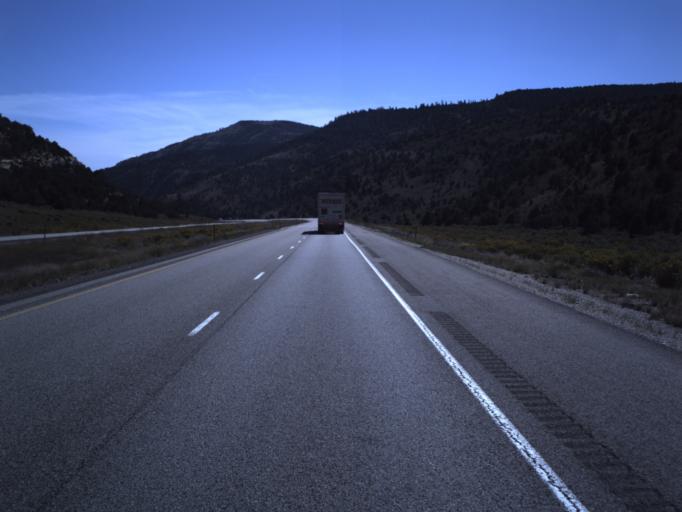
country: US
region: Utah
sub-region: Wayne County
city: Loa
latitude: 38.7657
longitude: -111.4682
